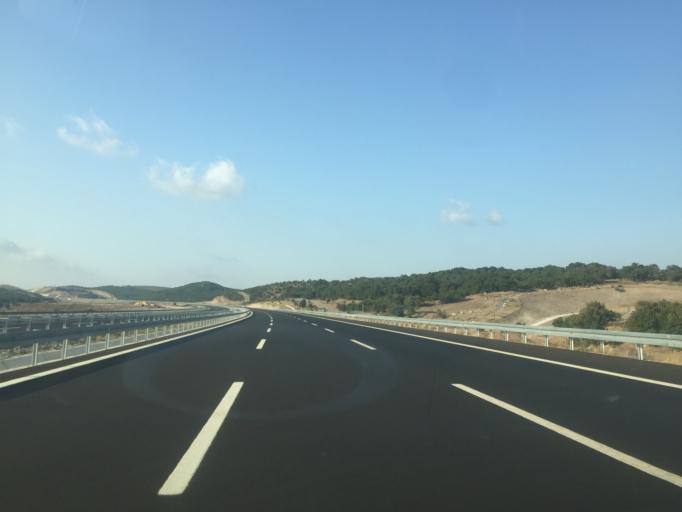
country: TR
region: Balikesir
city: Ertugrul
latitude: 39.5078
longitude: 27.6804
